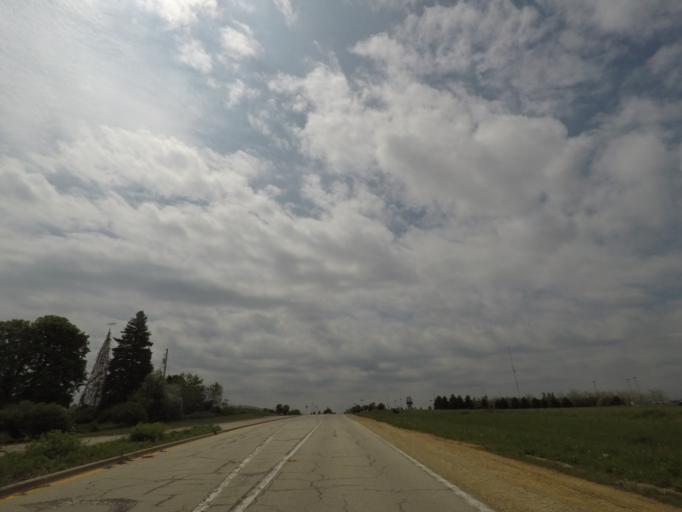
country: US
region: Illinois
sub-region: Winnebago County
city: Machesney Park
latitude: 42.3278
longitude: -88.9504
